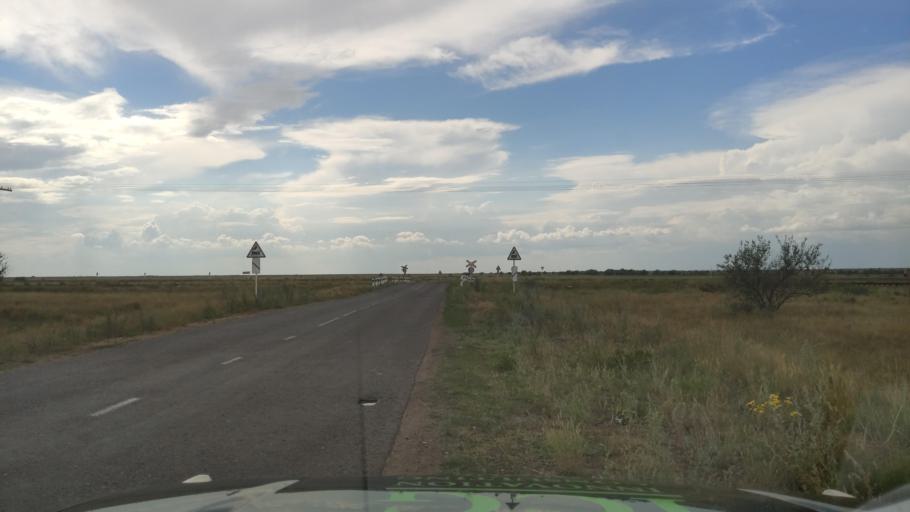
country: KZ
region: Pavlodar
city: Pavlodar
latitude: 52.6612
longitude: 77.4945
